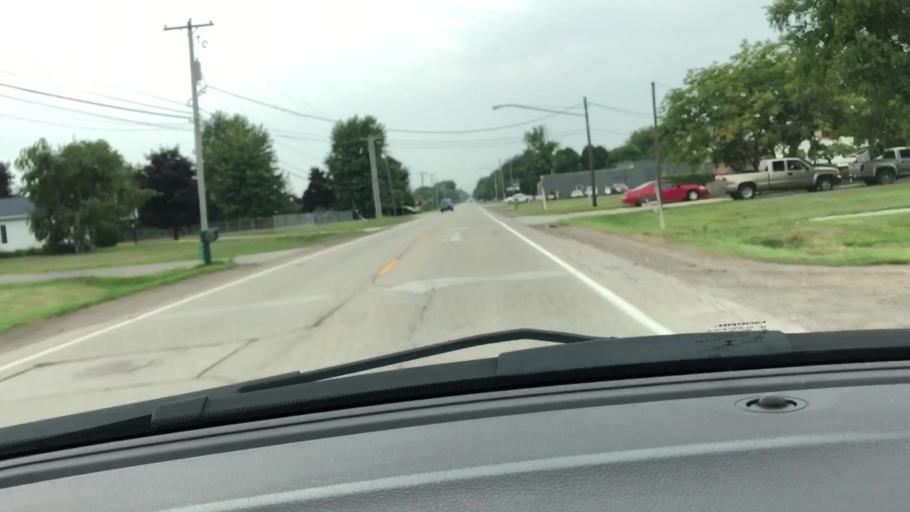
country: US
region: Michigan
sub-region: Bay County
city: Auburn
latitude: 43.6040
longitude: -84.1117
